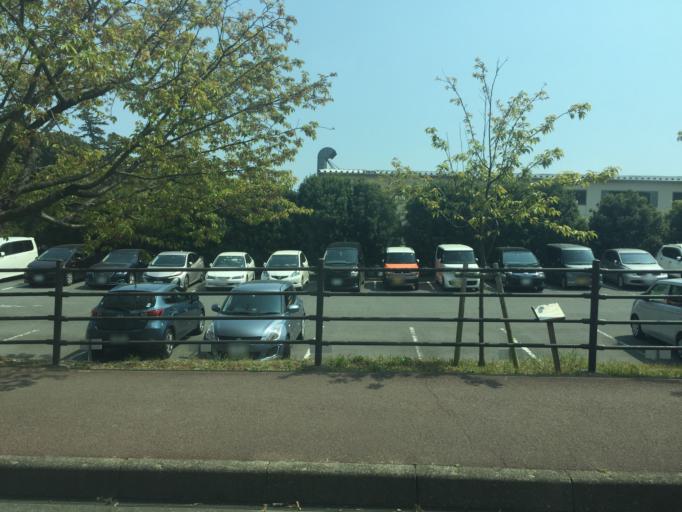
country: JP
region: Shizuoka
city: Ito
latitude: 34.8797
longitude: 139.1094
